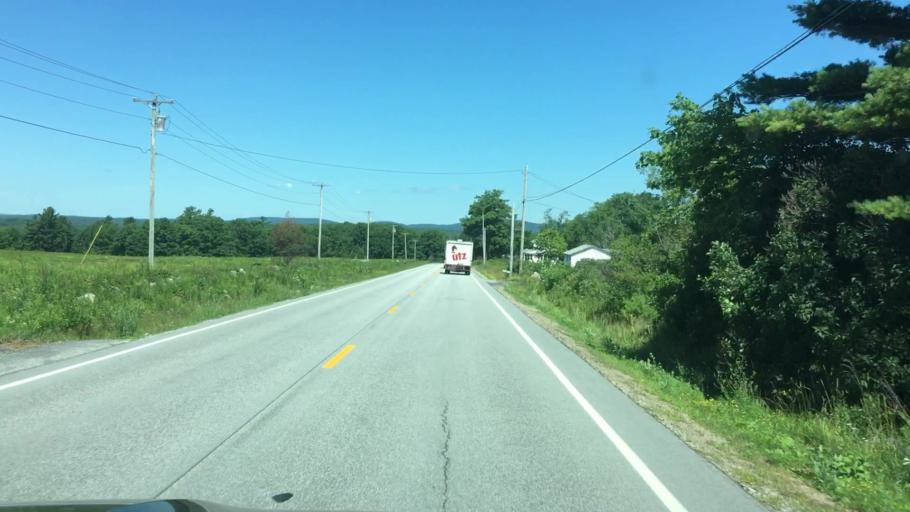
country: US
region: Maine
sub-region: Hancock County
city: Orland
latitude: 44.5508
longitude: -68.6919
